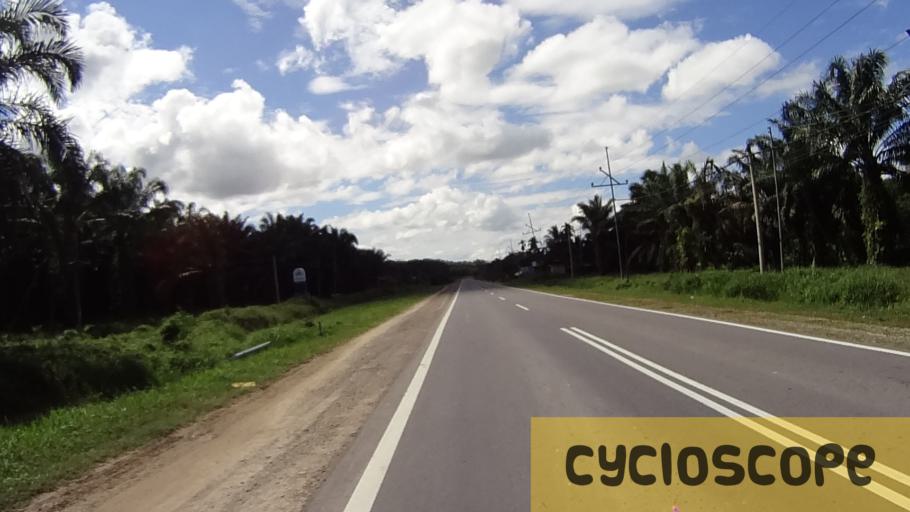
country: MY
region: Sabah
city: Beaufort
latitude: 5.3036
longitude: 115.6974
